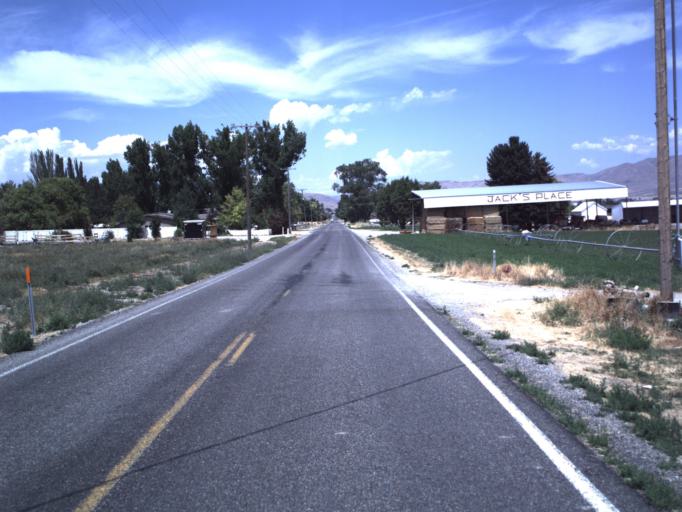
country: US
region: Utah
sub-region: Box Elder County
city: Tremonton
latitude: 41.6686
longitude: -112.2965
